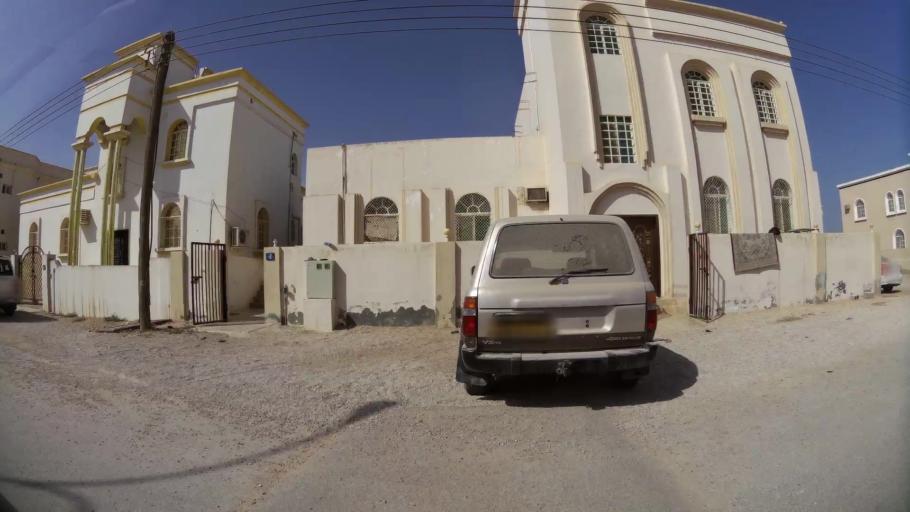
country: OM
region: Zufar
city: Salalah
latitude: 17.0002
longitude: 54.0154
